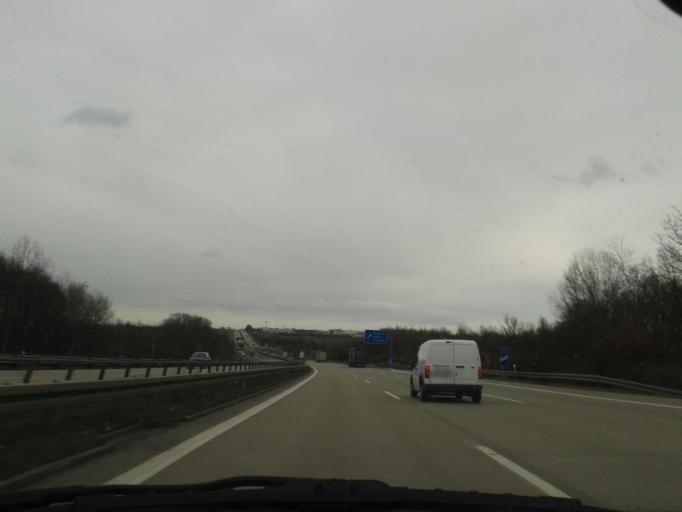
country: DE
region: Saxony
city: Wilsdruff
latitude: 51.0606
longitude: 13.5173
